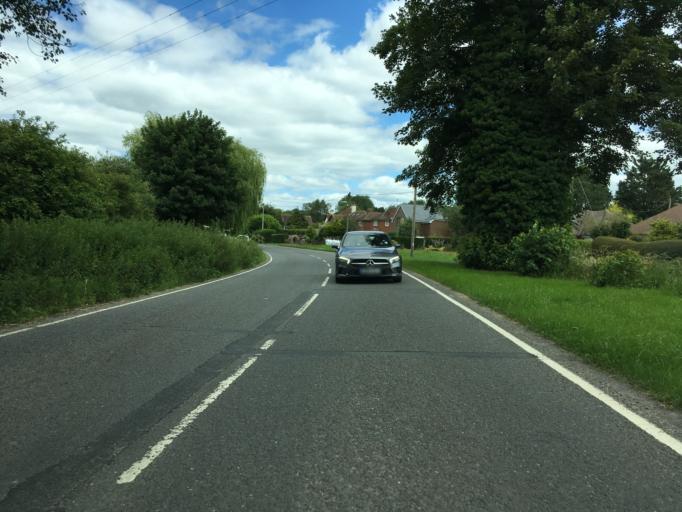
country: GB
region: England
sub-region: Hampshire
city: Overton
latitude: 51.2238
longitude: -1.3377
